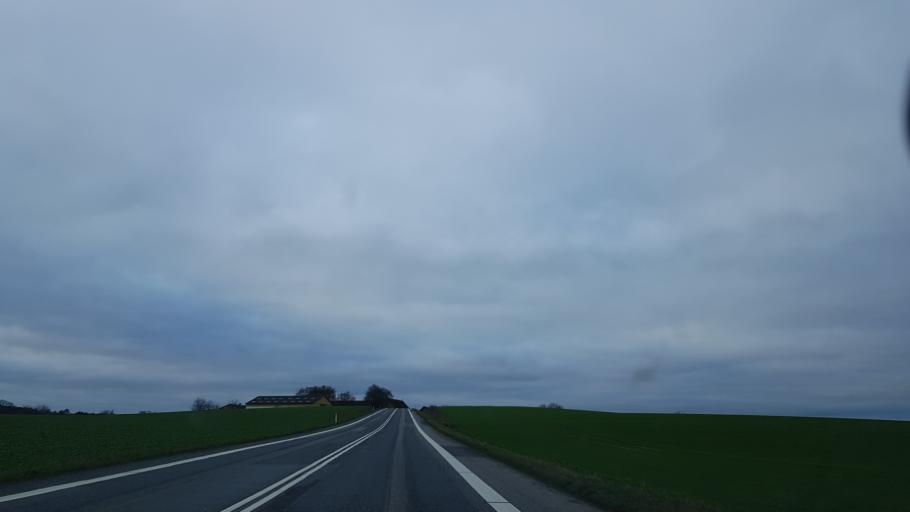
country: DK
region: Zealand
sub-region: Holbaek Kommune
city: Jyderup
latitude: 55.7093
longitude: 11.3748
